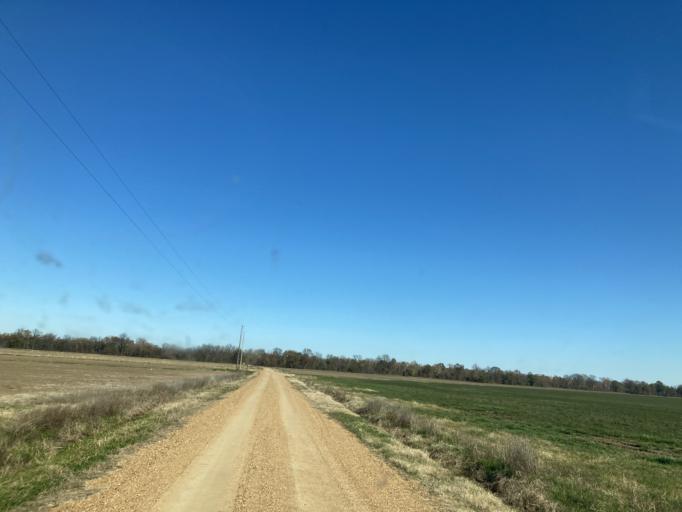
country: US
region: Mississippi
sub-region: Yazoo County
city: Yazoo City
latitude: 33.0088
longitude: -90.3812
